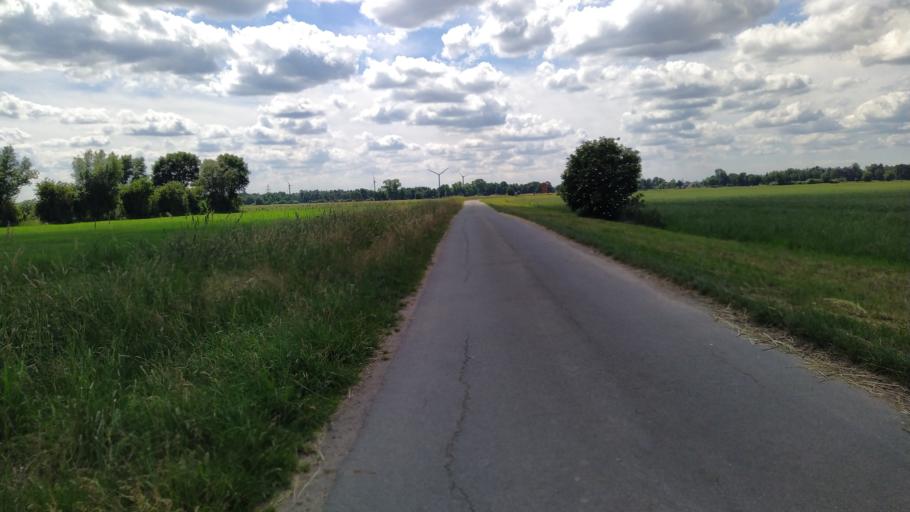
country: DE
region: Lower Saxony
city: Estorf
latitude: 53.5759
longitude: 9.1628
